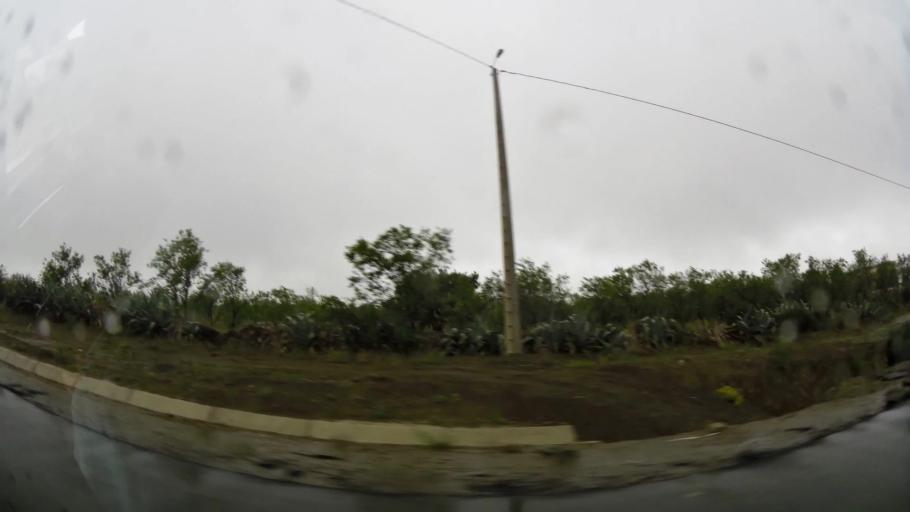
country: MA
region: Oriental
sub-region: Nador
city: Midar
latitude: 34.8474
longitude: -3.7216
